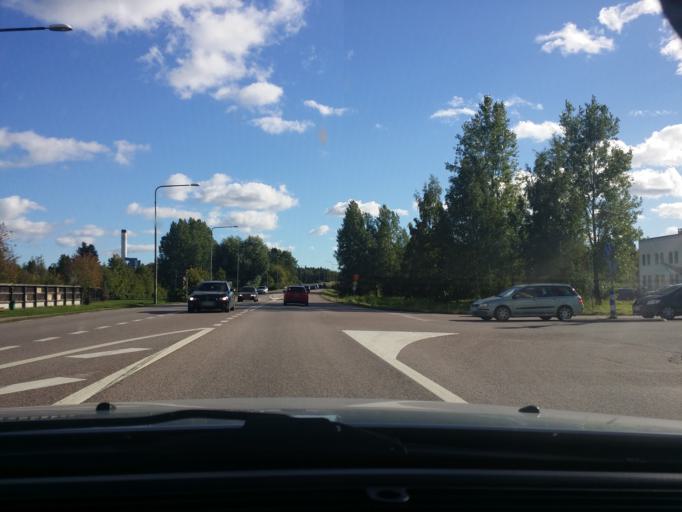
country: SE
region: Vaestmanland
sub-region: Vasteras
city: Vasteras
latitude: 59.5990
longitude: 16.4968
